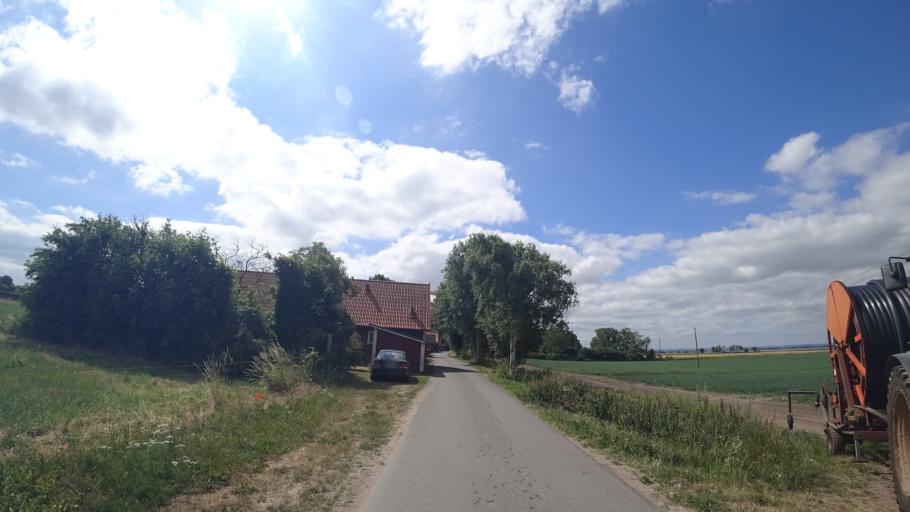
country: SE
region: Skane
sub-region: Kristianstads Kommun
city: Fjalkinge
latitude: 55.9850
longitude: 14.2670
